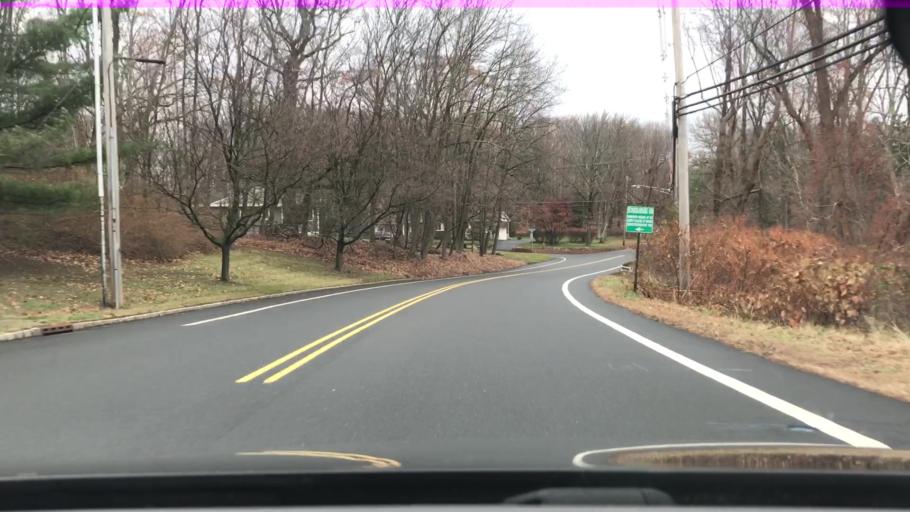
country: US
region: New Jersey
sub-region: Morris County
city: Randolph
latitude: 40.8412
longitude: -74.5708
